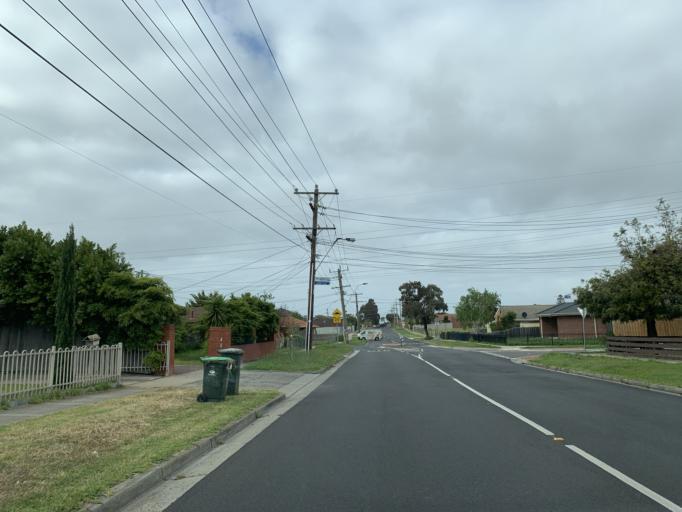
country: AU
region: Victoria
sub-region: Brimbank
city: St Albans
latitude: -37.7506
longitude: 144.8158
